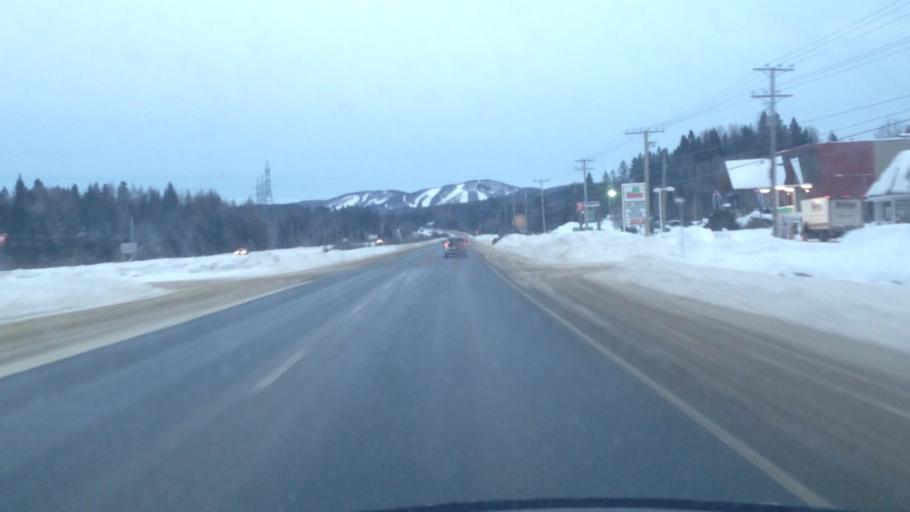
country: CA
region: Quebec
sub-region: Laurentides
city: Mont-Tremblant
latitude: 46.1164
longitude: -74.5530
